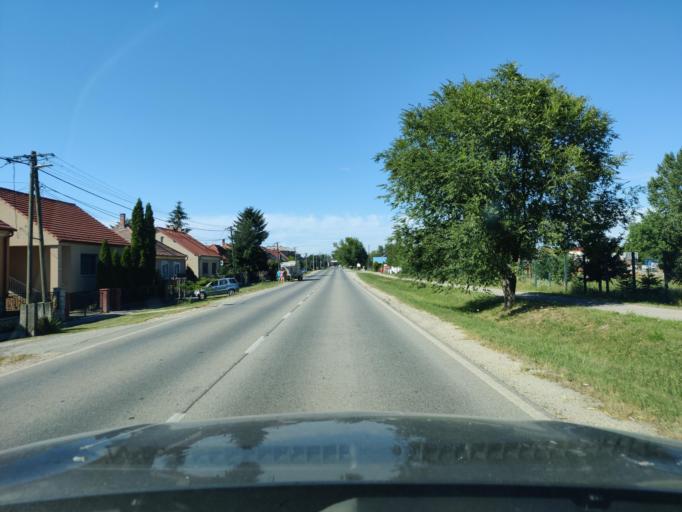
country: HU
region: Gyor-Moson-Sopron
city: Bosarkany
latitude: 47.6819
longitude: 17.2498
